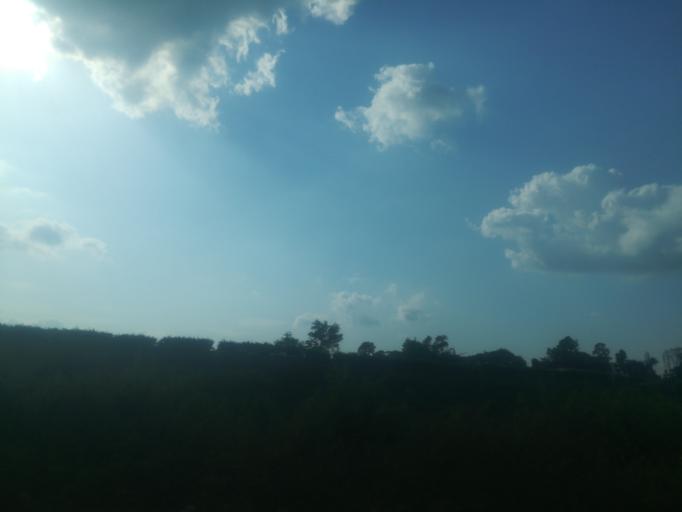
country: NG
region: Oyo
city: Moniya
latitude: 7.4902
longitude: 3.9168
